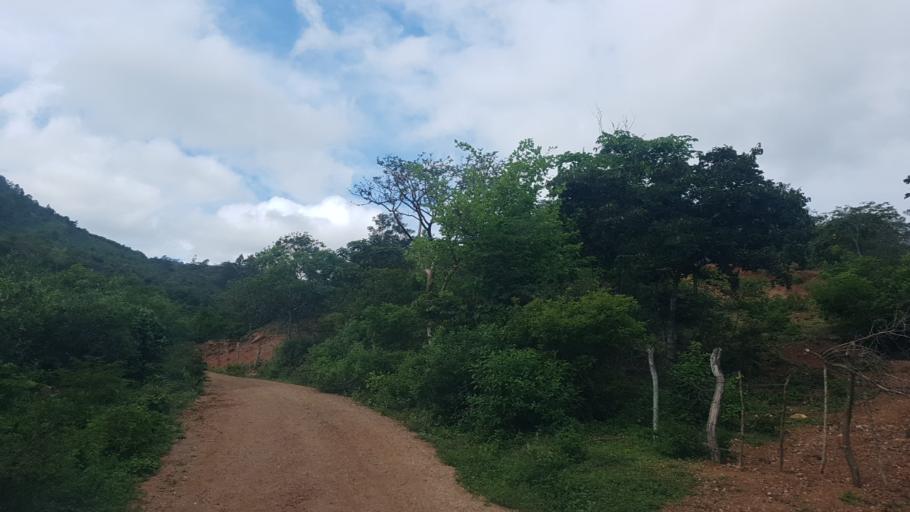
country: NI
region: Nueva Segovia
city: Ocotal
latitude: 13.6361
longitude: -86.6037
